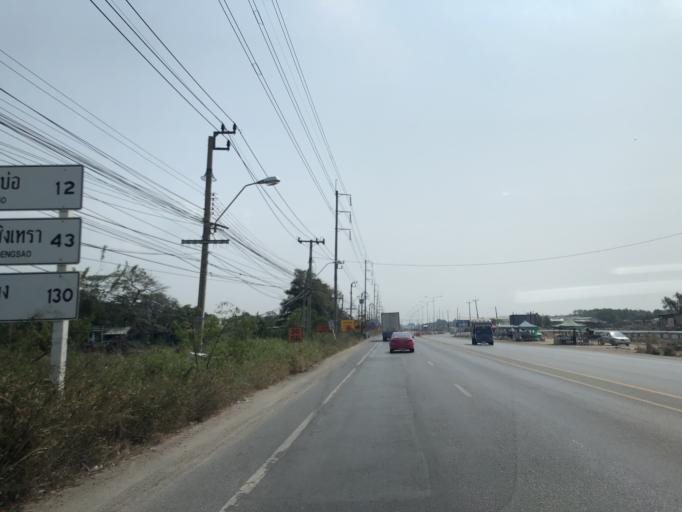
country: TH
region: Samut Prakan
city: Bang Bo District
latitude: 13.5125
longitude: 100.7915
